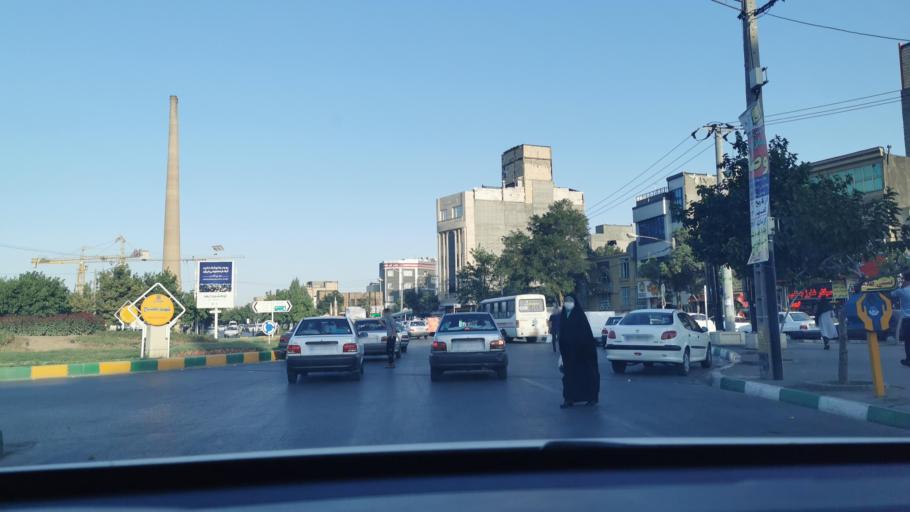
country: IR
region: Razavi Khorasan
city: Mashhad
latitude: 36.2907
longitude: 59.6488
